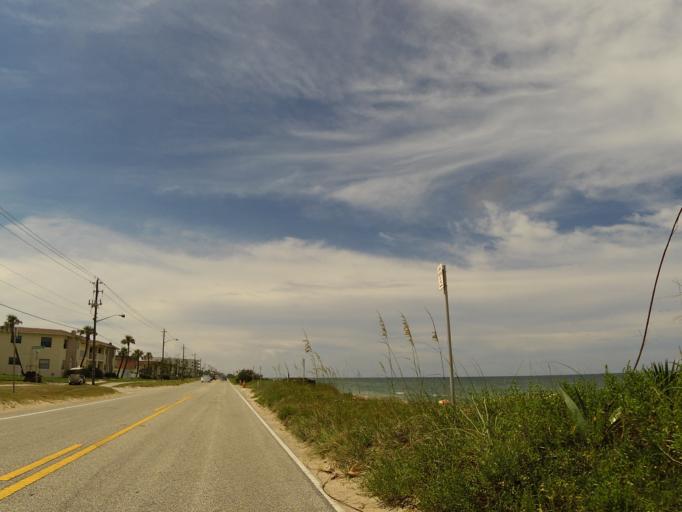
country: US
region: Florida
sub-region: Volusia County
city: Ormond-by-the-Sea
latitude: 29.3606
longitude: -81.0719
